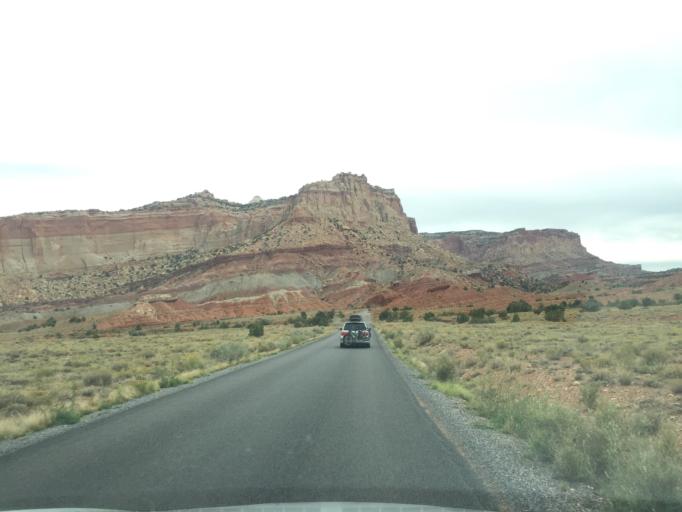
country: US
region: Utah
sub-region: Wayne County
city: Loa
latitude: 38.2588
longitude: -111.2365
